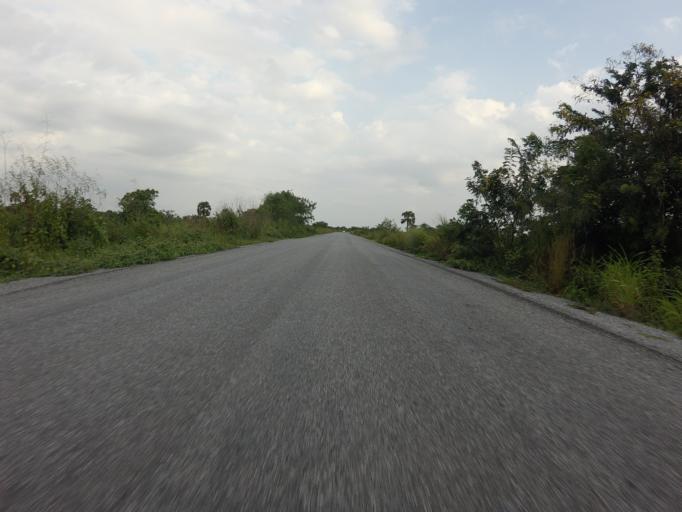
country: GH
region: Volta
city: Ho
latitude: 6.3839
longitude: 0.5298
